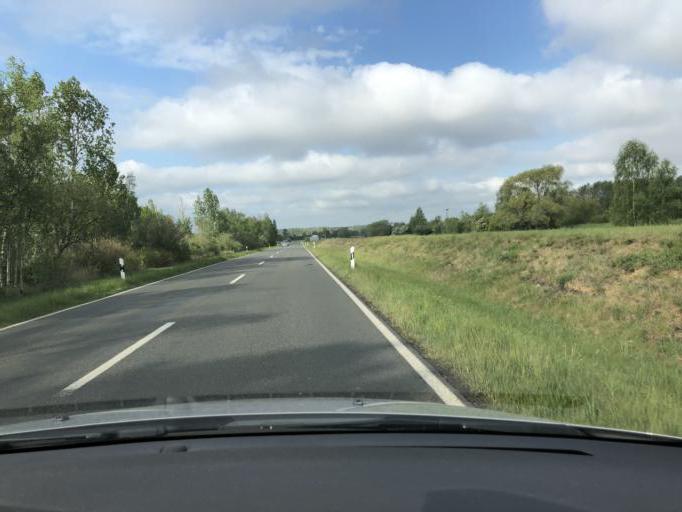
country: DE
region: Saxony
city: Deutzen
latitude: 51.1208
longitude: 12.4455
